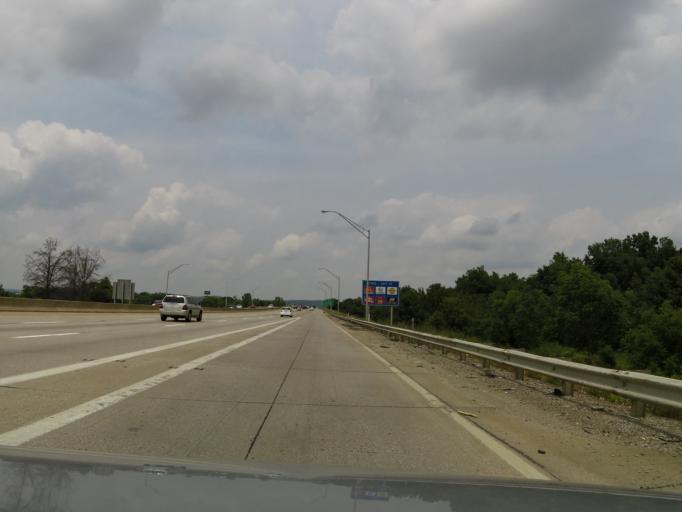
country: US
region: Kentucky
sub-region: Bullitt County
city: Shepherdsville
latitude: 37.9817
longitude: -85.6990
